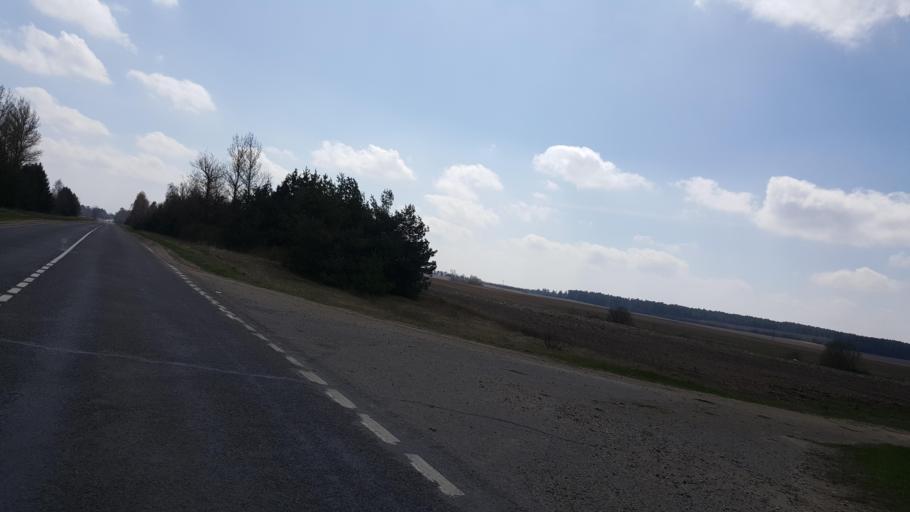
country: BY
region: Brest
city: Kamyanyets
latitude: 52.3547
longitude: 23.8965
